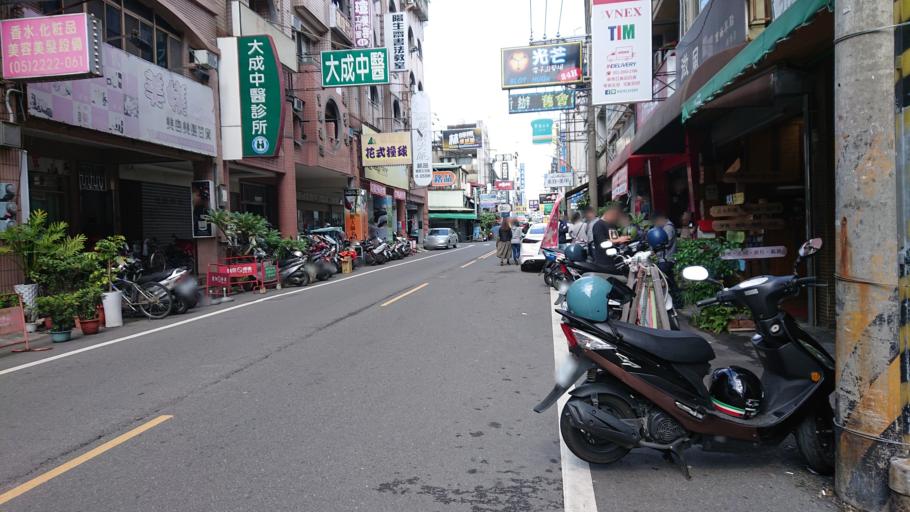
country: TW
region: Taiwan
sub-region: Chiayi
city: Jiayi Shi
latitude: 23.4782
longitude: 120.4442
